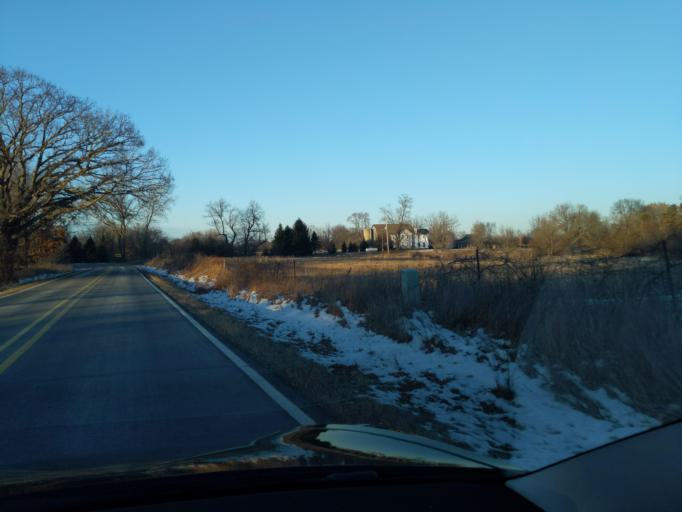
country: US
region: Michigan
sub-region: Ingham County
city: Stockbridge
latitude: 42.4905
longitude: -84.2180
